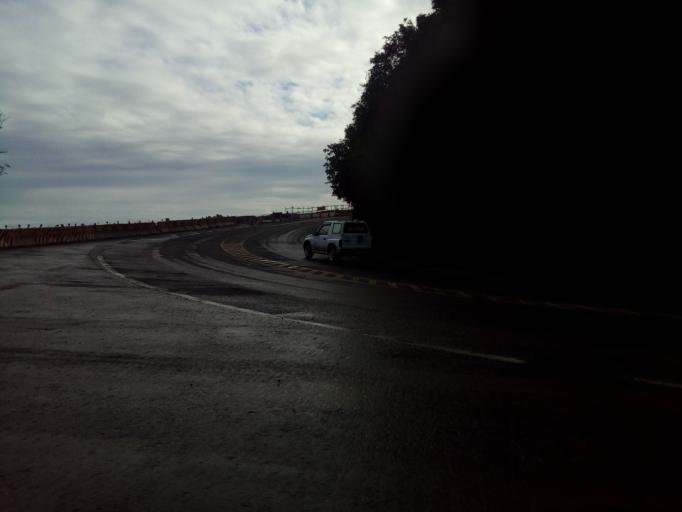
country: TW
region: Taiwan
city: Taitung City
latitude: 22.5624
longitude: 120.9782
